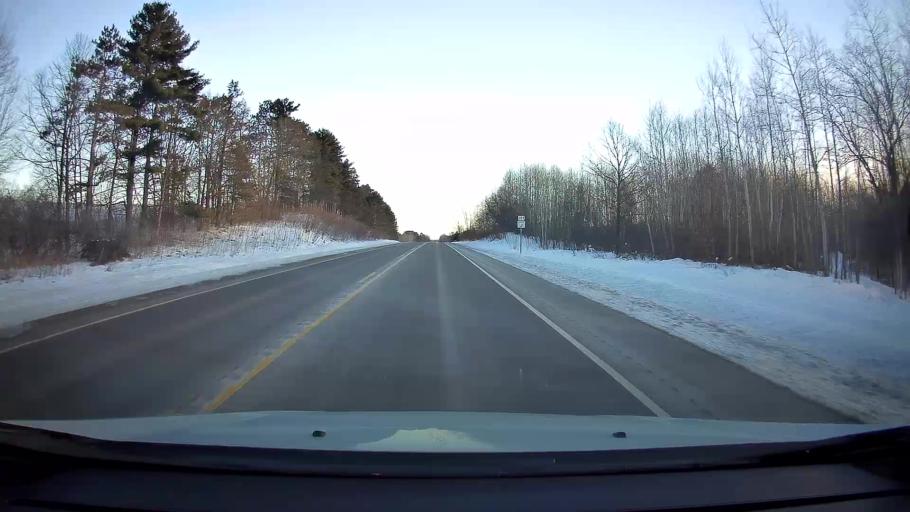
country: US
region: Wisconsin
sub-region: Washburn County
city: Shell Lake
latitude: 45.6802
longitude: -91.9854
